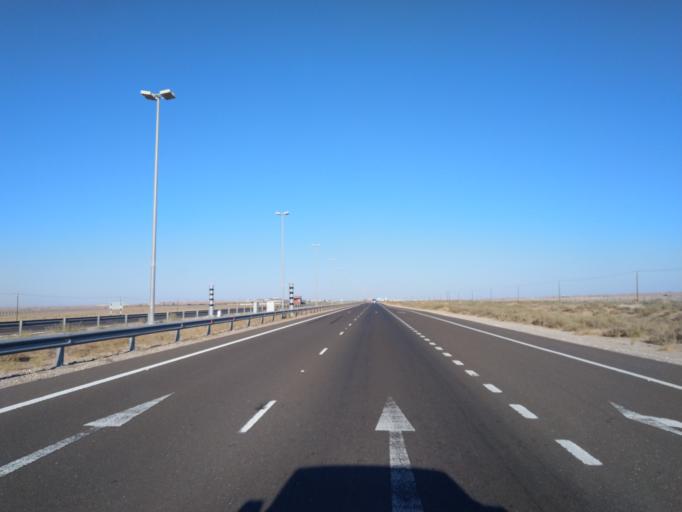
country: OM
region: Al Buraimi
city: Al Buraymi
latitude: 24.4978
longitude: 55.4339
